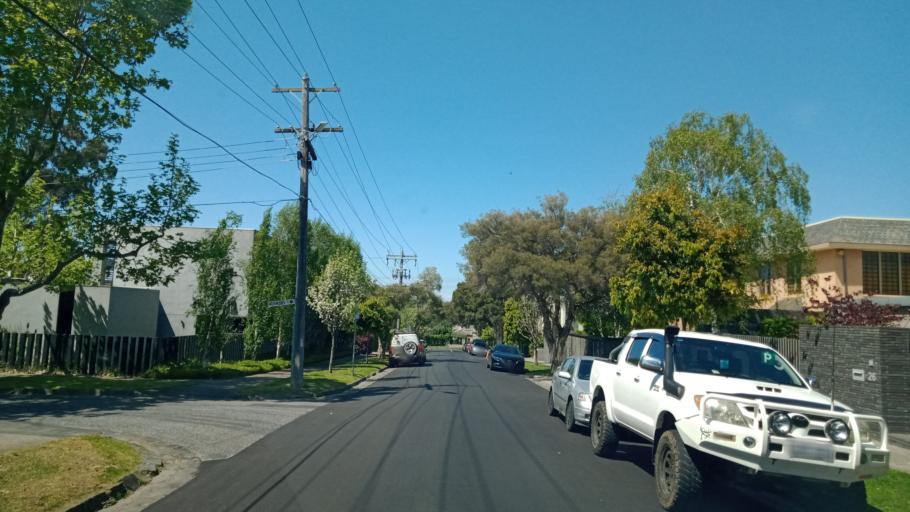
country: AU
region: Victoria
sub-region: Stonnington
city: Glen Iris
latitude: -37.8501
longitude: 145.0390
